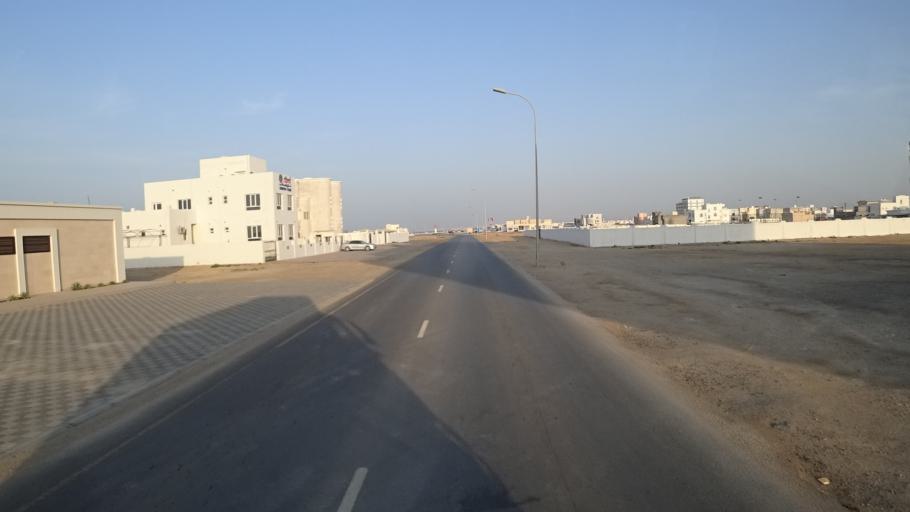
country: OM
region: Ash Sharqiyah
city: Sur
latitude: 22.6055
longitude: 59.4775
